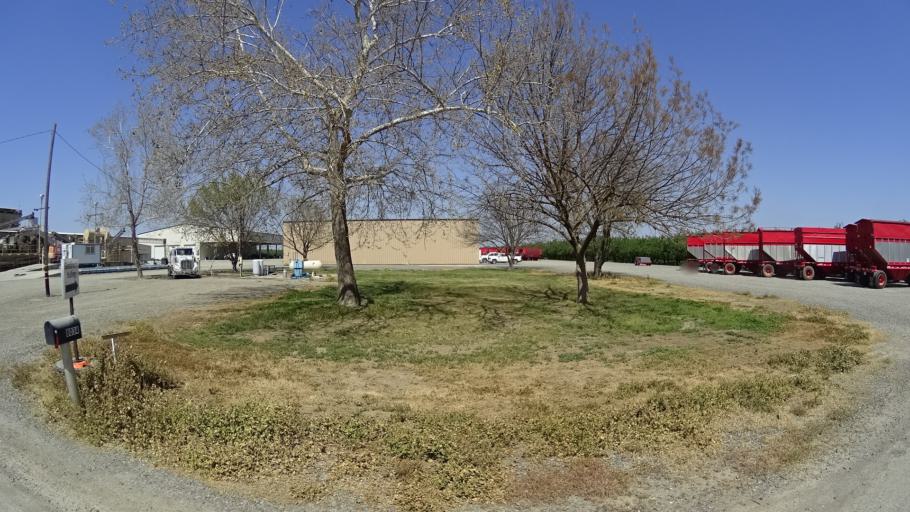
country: US
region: California
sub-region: Glenn County
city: Willows
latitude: 39.5363
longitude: -122.0234
